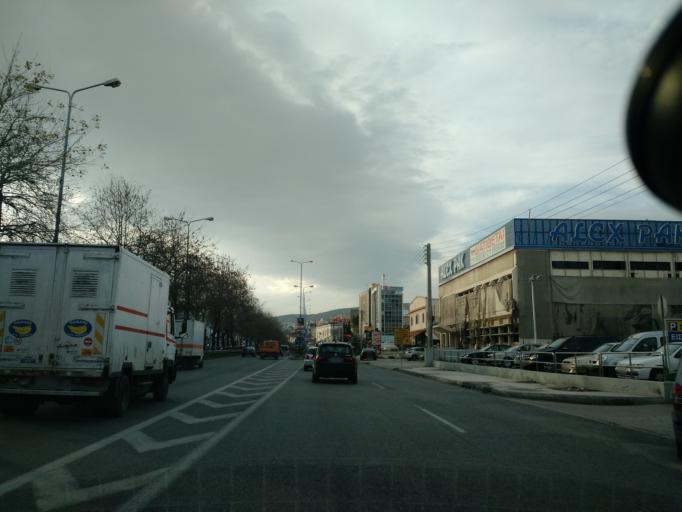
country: GR
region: Attica
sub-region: Nomarchia Athinas
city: Peristeri
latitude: 37.9999
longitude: 23.6888
